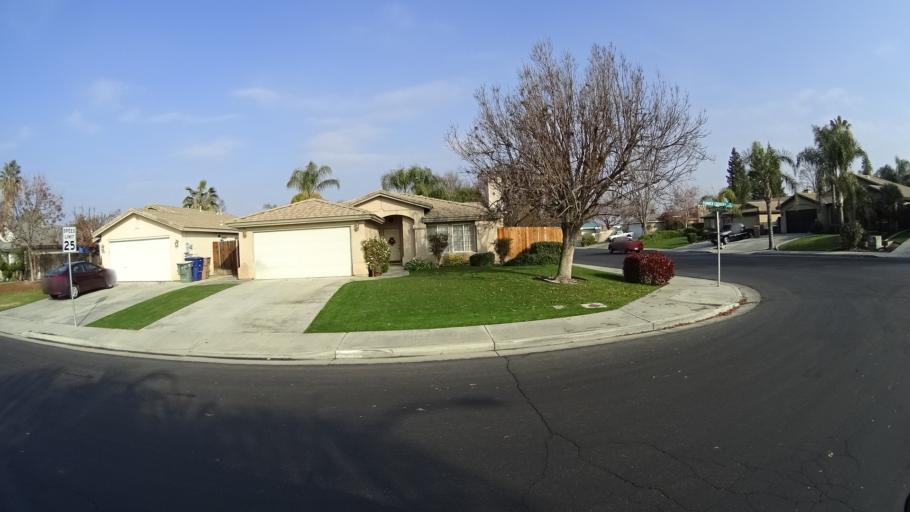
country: US
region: California
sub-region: Kern County
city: Greenfield
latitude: 35.3004
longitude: -119.0658
